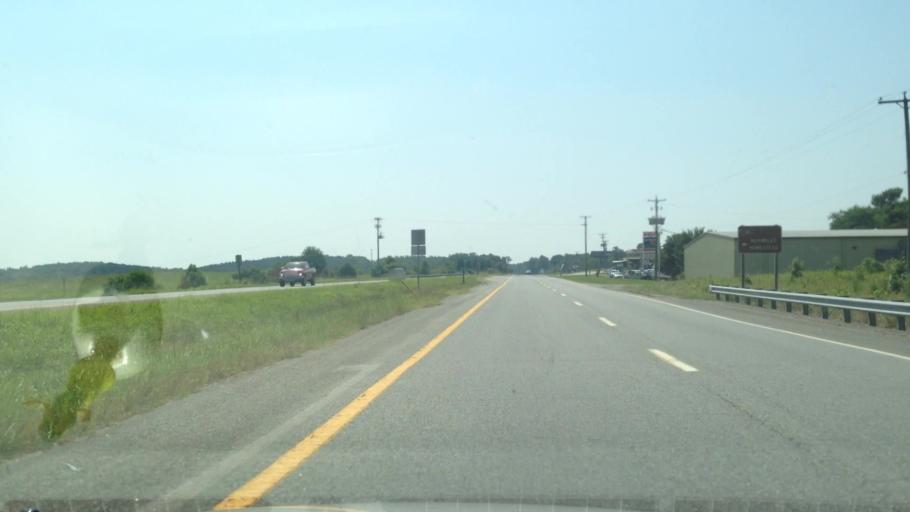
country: US
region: Virginia
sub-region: Patrick County
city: Patrick Springs
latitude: 36.6008
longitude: -80.1598
